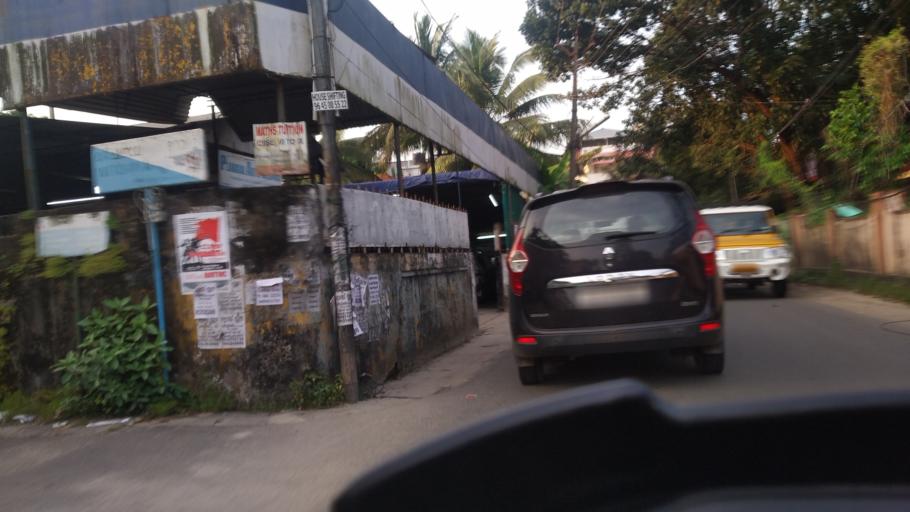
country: IN
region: Kerala
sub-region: Ernakulam
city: Elur
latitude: 10.0212
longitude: 76.3007
